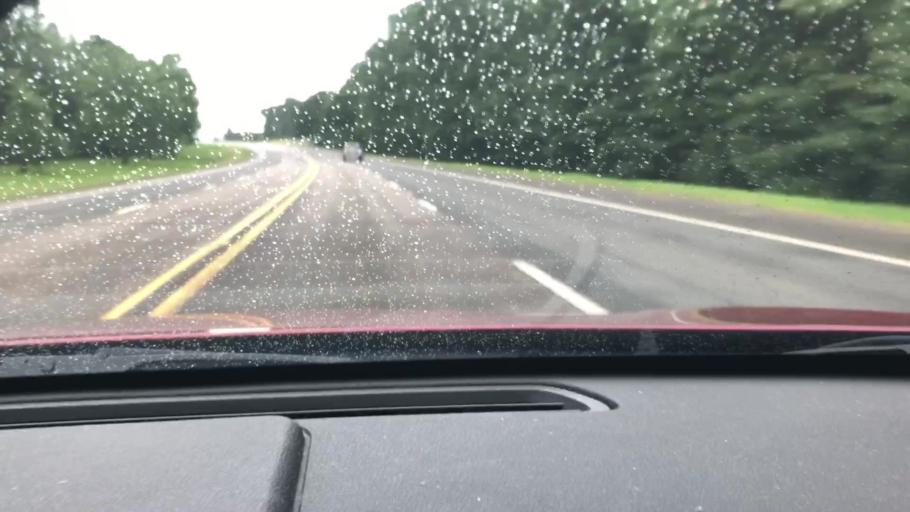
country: US
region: Arkansas
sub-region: Lafayette County
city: Lewisville
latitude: 33.3557
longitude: -93.5645
